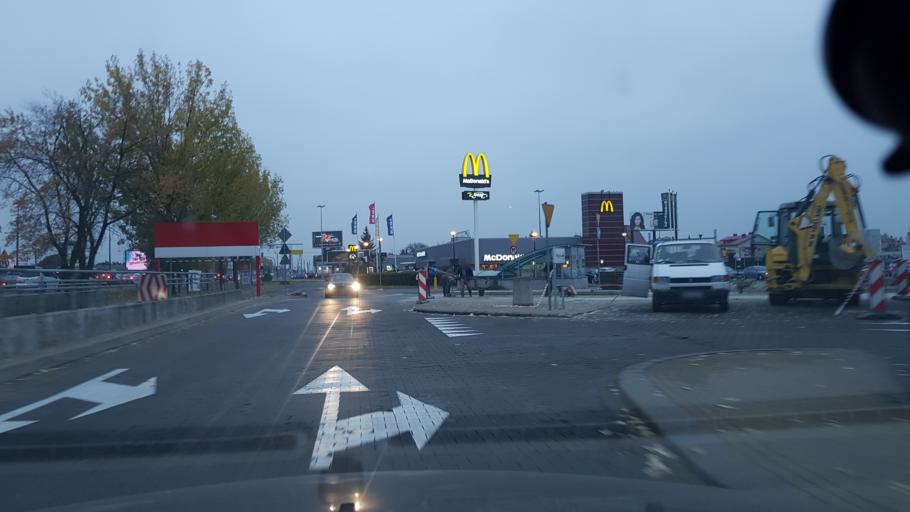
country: PL
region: Masovian Voivodeship
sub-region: Powiat pruszkowski
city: Nowe Grocholice
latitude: 52.1336
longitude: 20.8981
